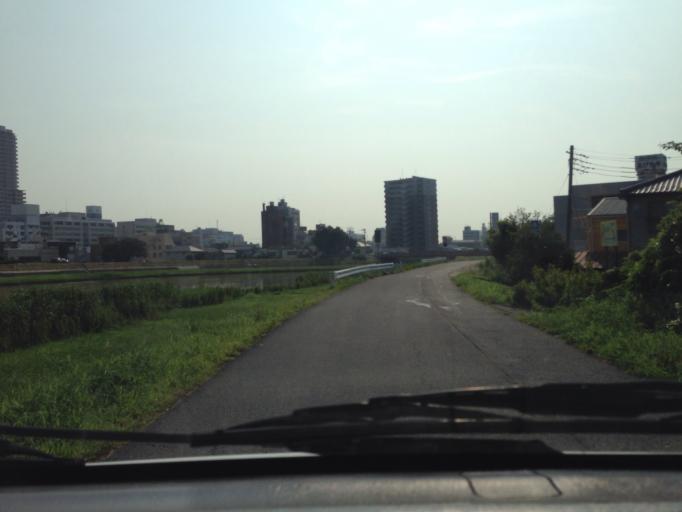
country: JP
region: Ibaraki
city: Naka
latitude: 36.0760
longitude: 140.1986
